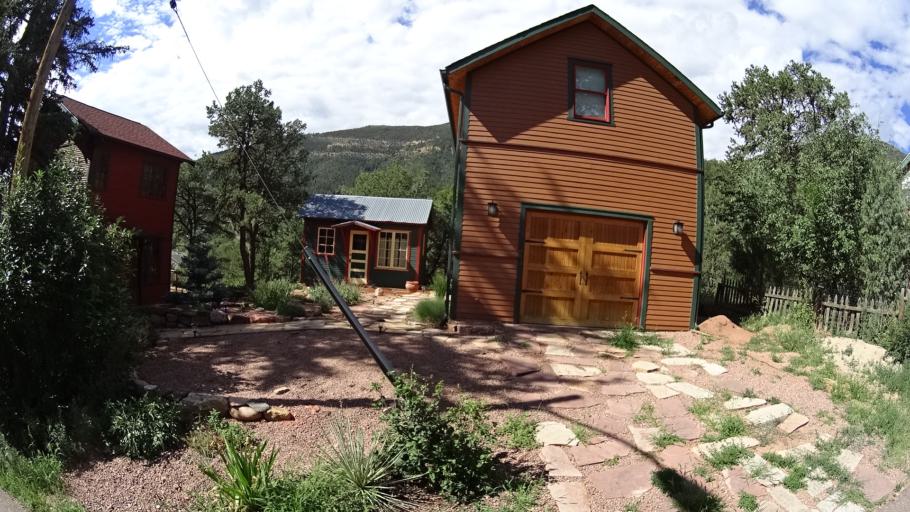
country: US
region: Colorado
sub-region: El Paso County
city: Manitou Springs
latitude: 38.8615
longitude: -104.9250
